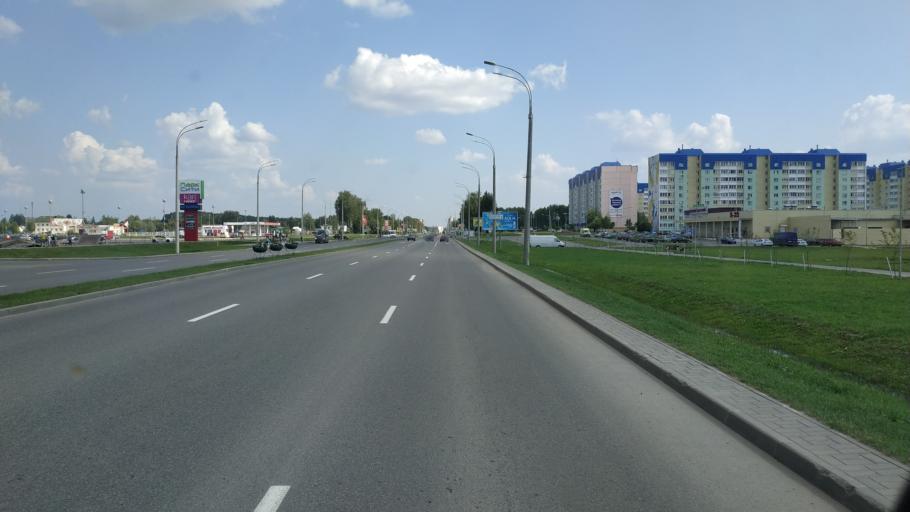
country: BY
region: Mogilev
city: Buynichy
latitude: 53.9348
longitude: 30.2536
